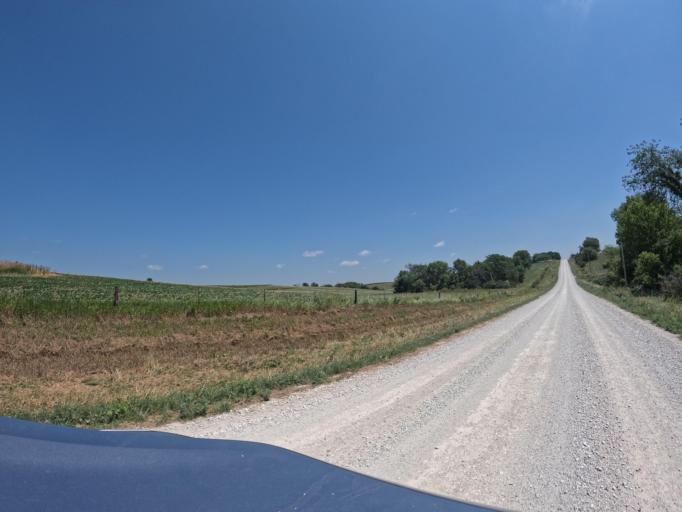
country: US
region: Iowa
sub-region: Keokuk County
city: Sigourney
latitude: 41.2579
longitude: -92.1678
